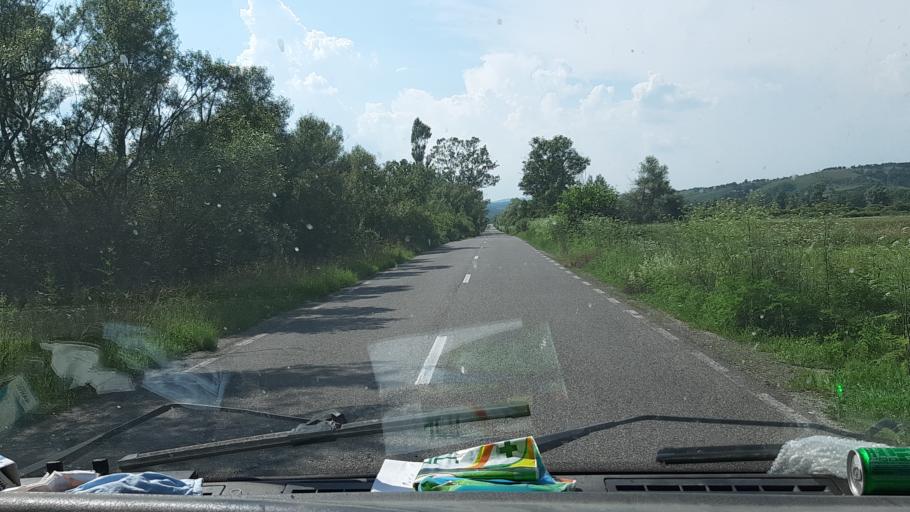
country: RO
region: Caras-Severin
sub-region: Comuna Ezeris
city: Ezeris
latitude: 45.4002
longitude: 21.9112
